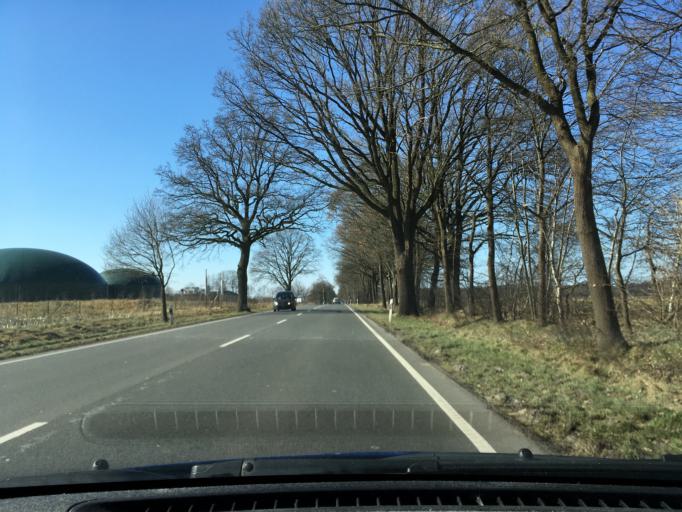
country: DE
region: Lower Saxony
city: Botersen
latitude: 53.1207
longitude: 9.3139
